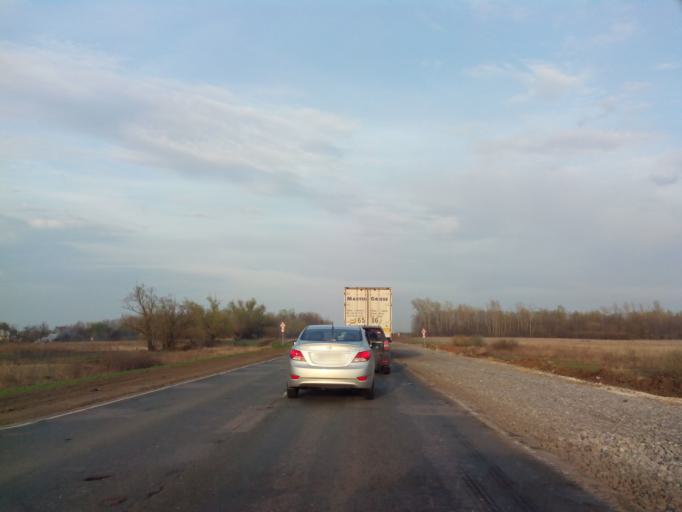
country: RU
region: Rjazan
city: Zarechnyy
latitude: 53.7522
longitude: 39.8268
